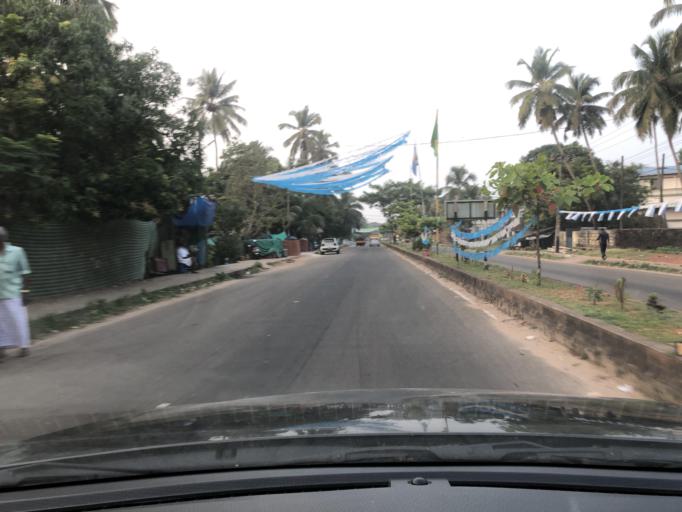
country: IN
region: Kerala
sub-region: Kozhikode
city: Kozhikode
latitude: 11.2993
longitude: 75.7557
